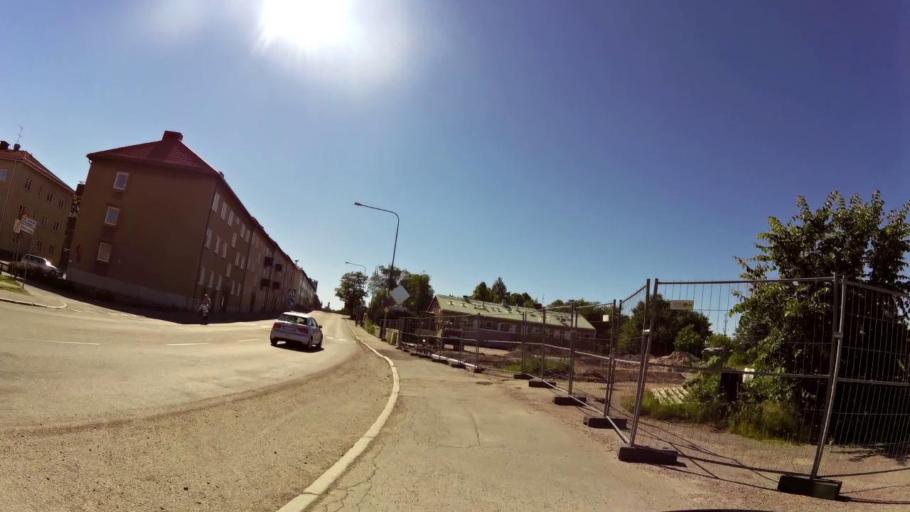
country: SE
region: OEstergoetland
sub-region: Linkopings Kommun
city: Linkoping
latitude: 58.4127
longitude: 15.6400
